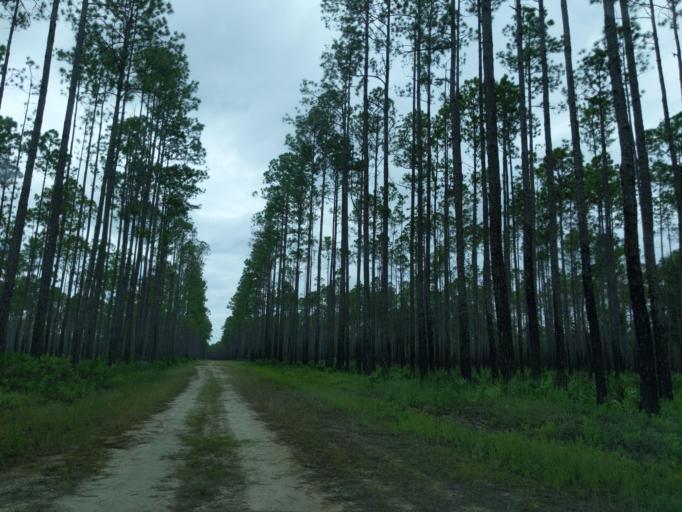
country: US
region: Florida
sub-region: Gadsden County
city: Midway
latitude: 30.3757
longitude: -84.4875
